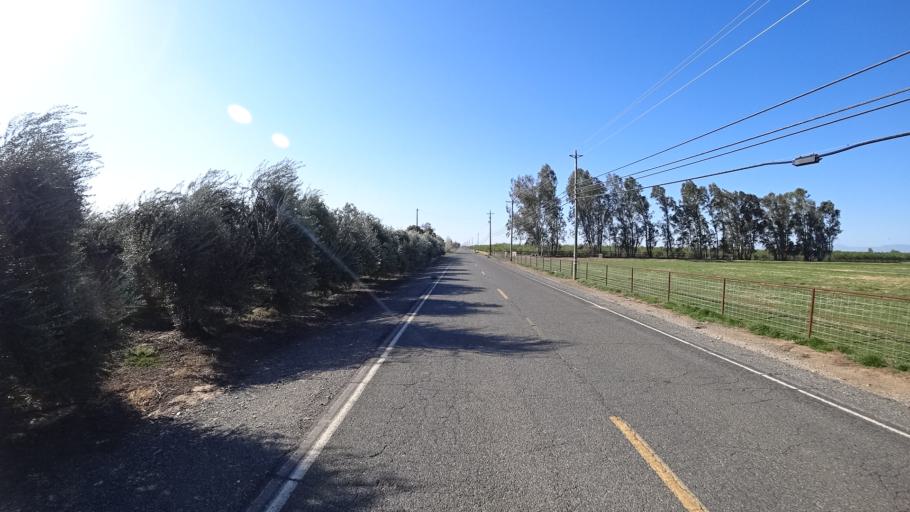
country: US
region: California
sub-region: Glenn County
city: Orland
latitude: 39.7871
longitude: -122.1041
